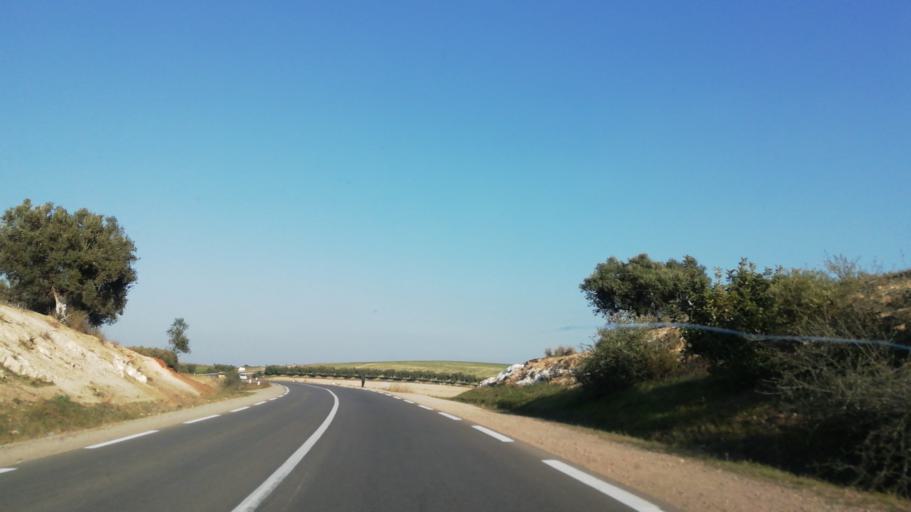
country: DZ
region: Sidi Bel Abbes
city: Sidi Bel Abbes
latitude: 35.1632
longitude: -0.8642
